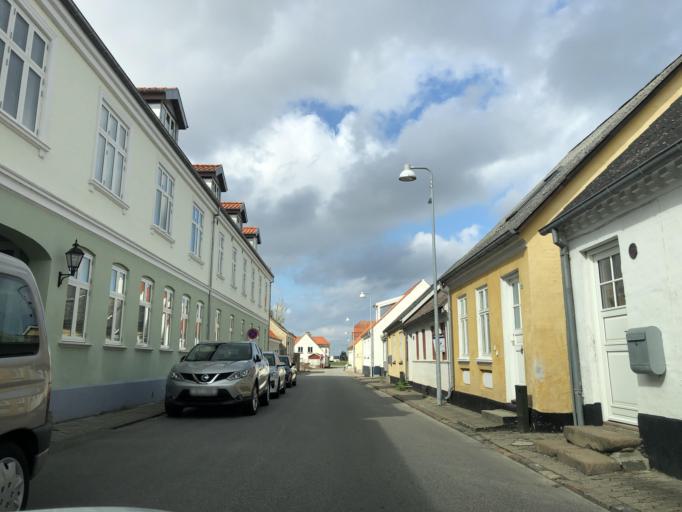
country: DK
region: North Denmark
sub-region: Alborg Kommune
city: Nibe
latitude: 56.9834
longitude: 9.6358
